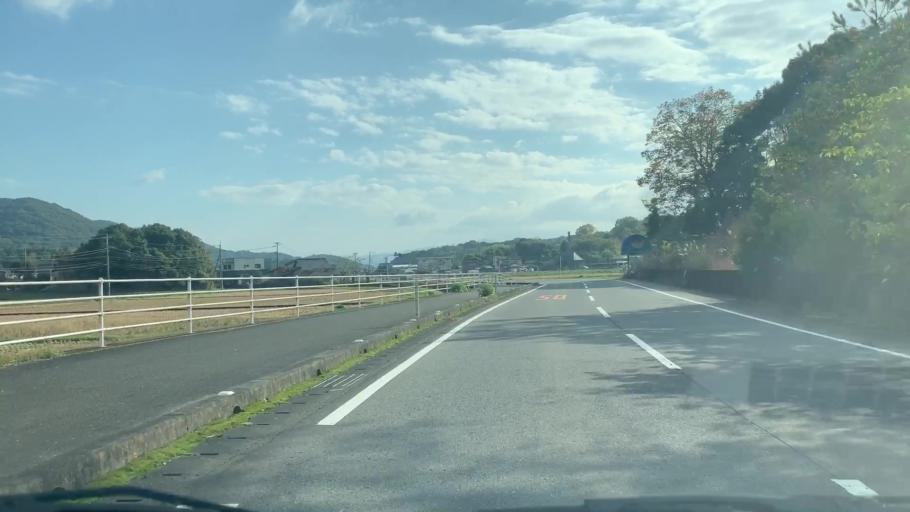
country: JP
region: Saga Prefecture
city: Takeocho-takeo
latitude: 33.1614
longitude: 130.0614
